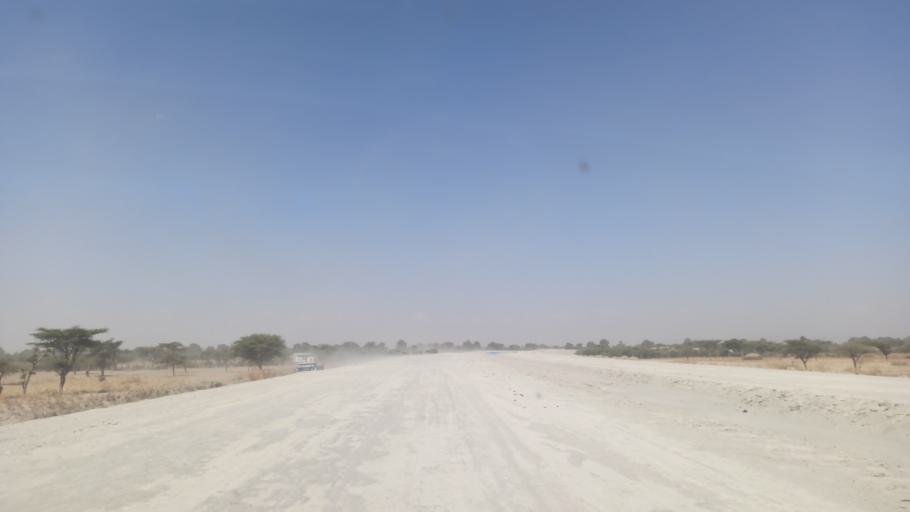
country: ET
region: Oromiya
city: Ziway
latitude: 7.6957
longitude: 38.6467
